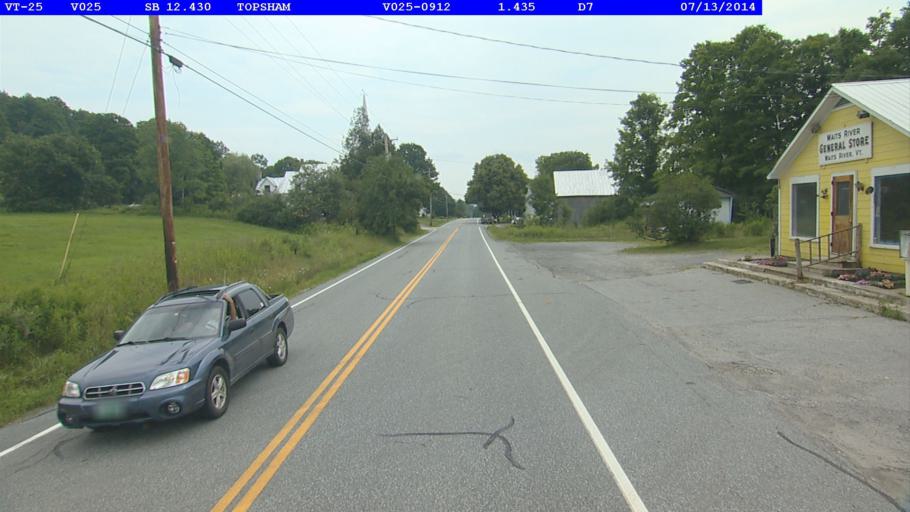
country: US
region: Vermont
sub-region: Orange County
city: Chelsea
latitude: 44.0902
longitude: -72.2837
